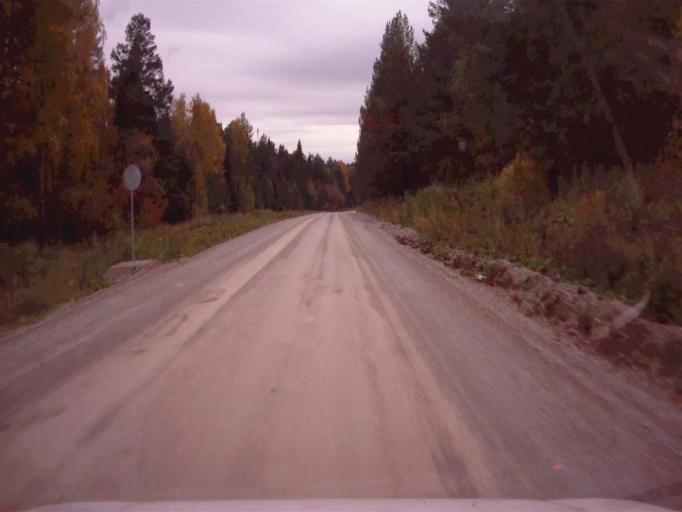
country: RU
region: Chelyabinsk
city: Nyazepetrovsk
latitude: 56.0508
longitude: 59.5318
